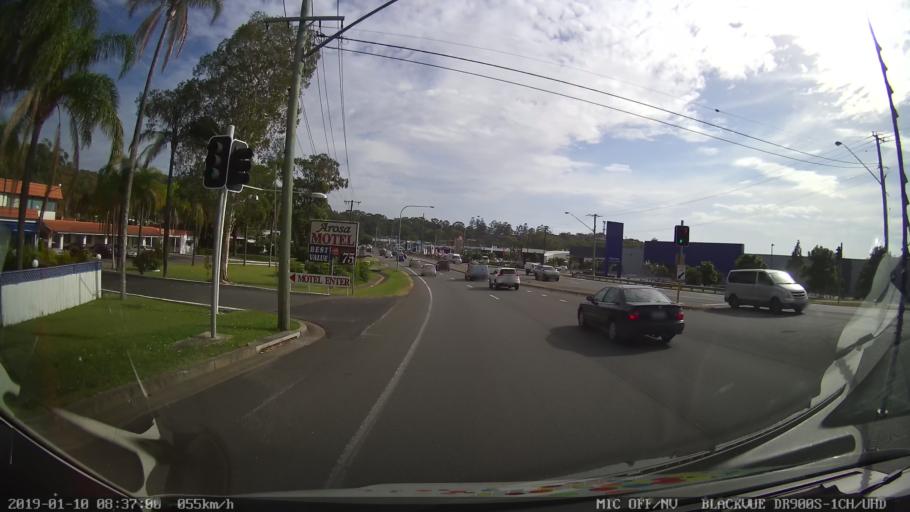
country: AU
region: New South Wales
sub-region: Coffs Harbour
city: Coffs Harbour
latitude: -30.3084
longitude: 153.1004
